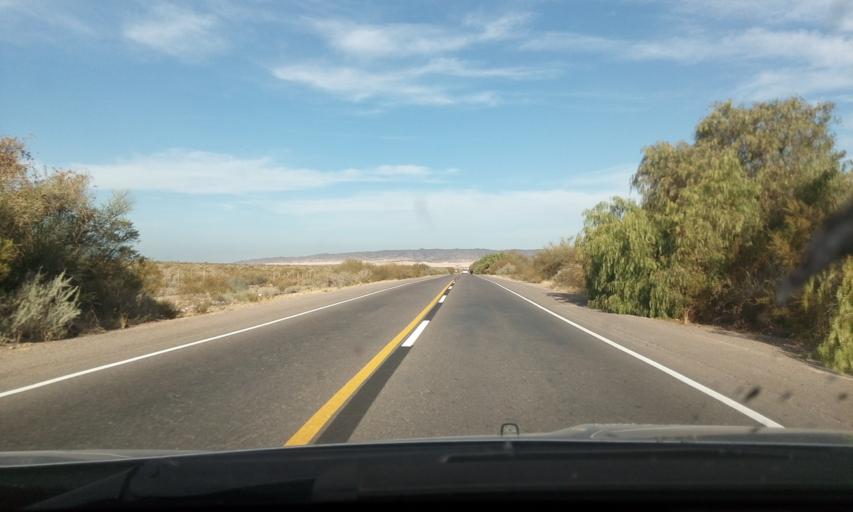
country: AR
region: San Juan
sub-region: Departamento de Rivadavia
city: Rivadavia
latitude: -31.4318
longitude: -68.6643
